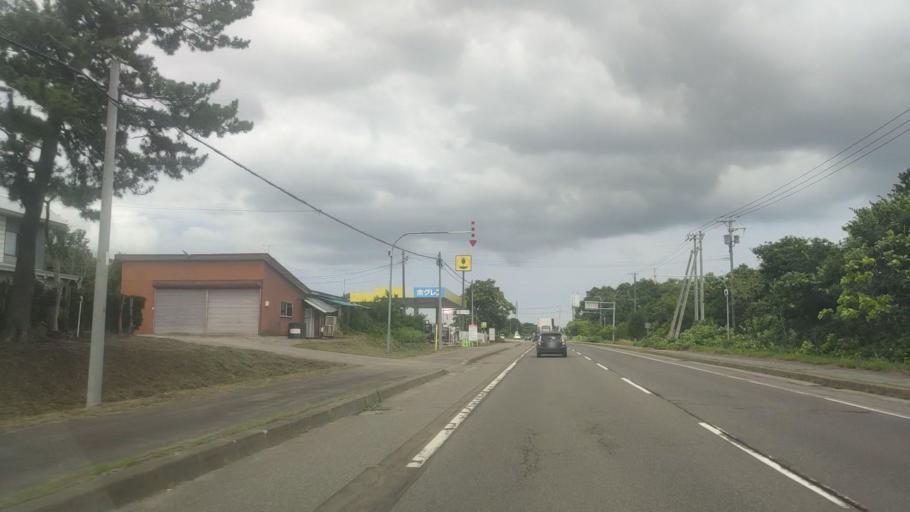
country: JP
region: Hokkaido
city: Nanae
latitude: 42.0880
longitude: 140.5824
